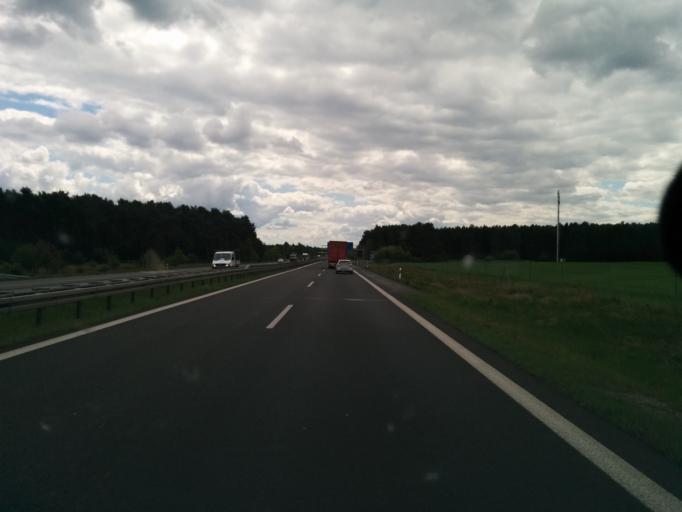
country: DE
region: Brandenburg
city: Gross Kreutz
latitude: 52.3498
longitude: 12.8152
